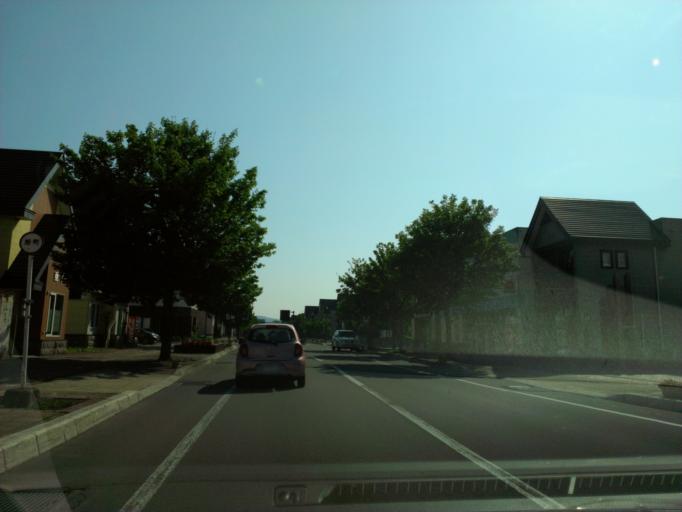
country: JP
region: Hokkaido
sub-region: Asahikawa-shi
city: Asahikawa
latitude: 43.5938
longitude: 142.4670
